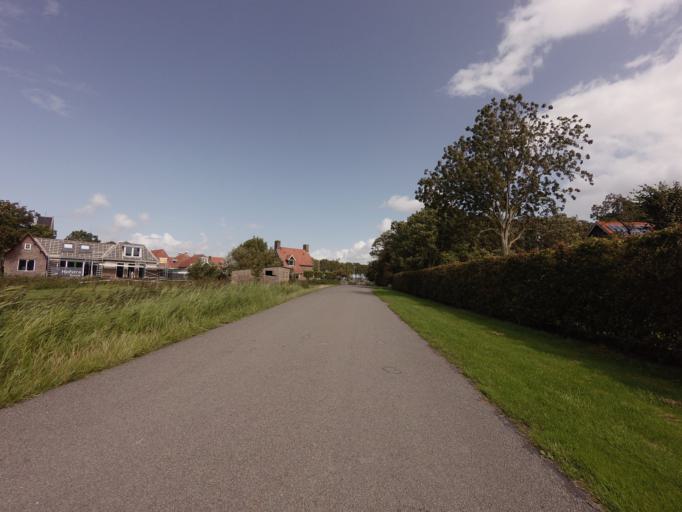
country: NL
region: Friesland
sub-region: Gemeente Harlingen
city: Harlingen
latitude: 53.1136
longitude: 5.4409
